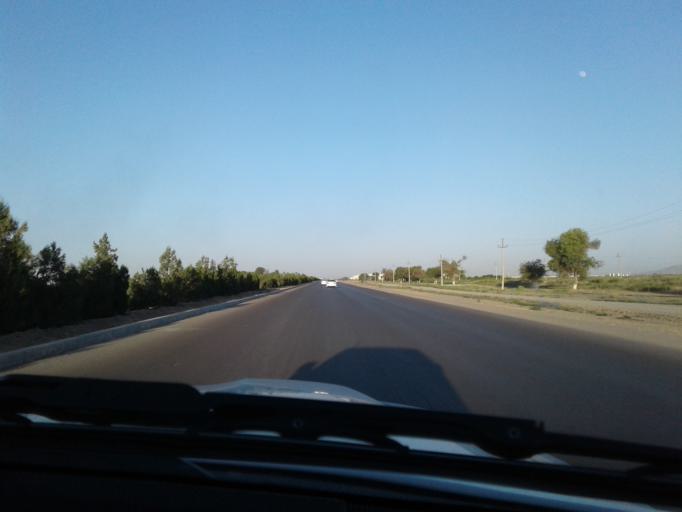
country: TM
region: Ahal
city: Abadan
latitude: 38.1725
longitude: 57.9073
